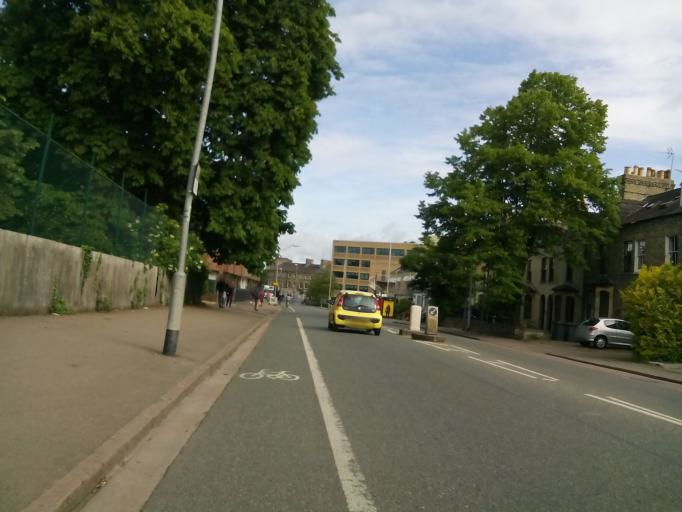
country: GB
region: England
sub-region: Cambridgeshire
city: Cambridge
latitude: 52.1934
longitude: 0.1328
